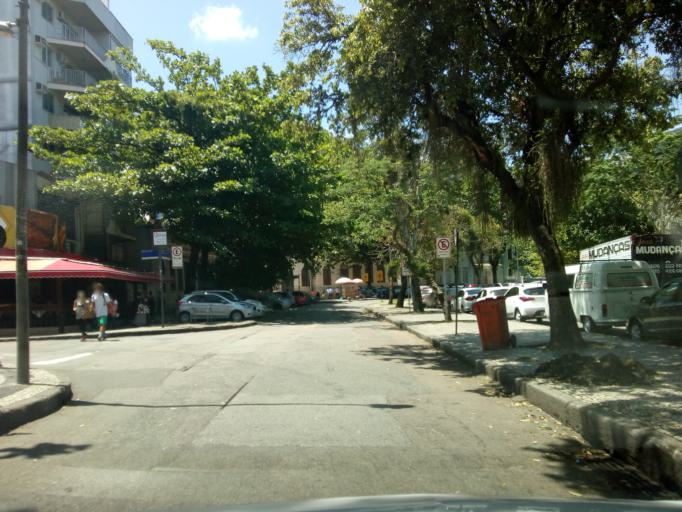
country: BR
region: Rio de Janeiro
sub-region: Rio De Janeiro
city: Rio de Janeiro
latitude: -22.9741
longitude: -43.2270
